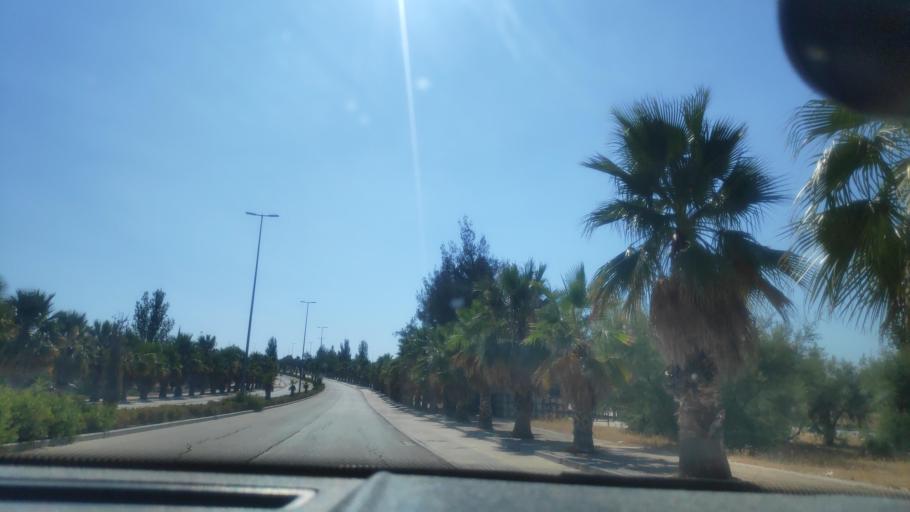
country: ES
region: Andalusia
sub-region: Provincia de Jaen
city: Jaen
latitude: 37.8284
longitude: -3.7711
